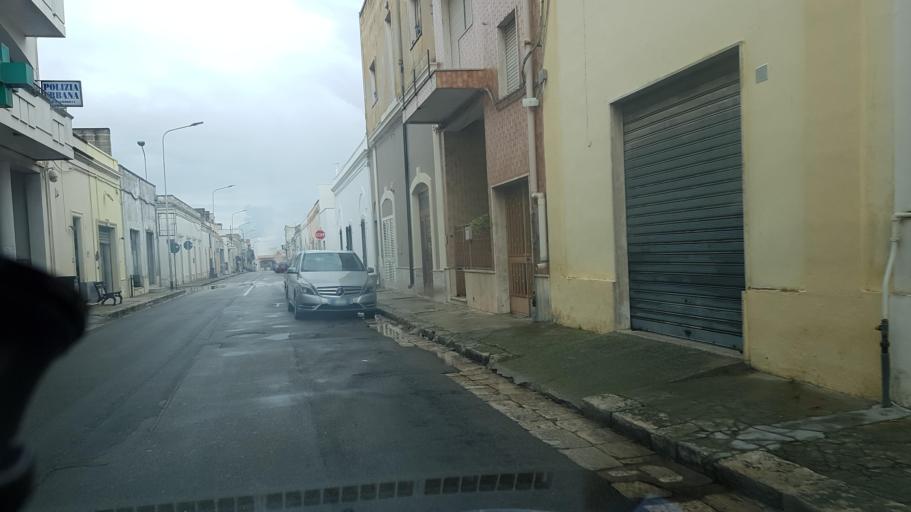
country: IT
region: Apulia
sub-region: Provincia di Lecce
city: Carmiano
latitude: 40.3459
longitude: 18.0424
